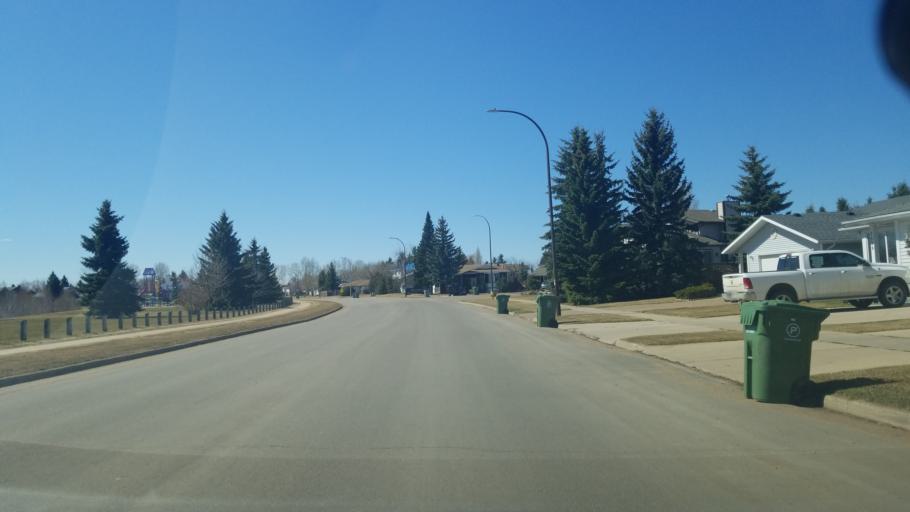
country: CA
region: Saskatchewan
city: Lloydminster
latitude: 53.2630
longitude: -110.0110
